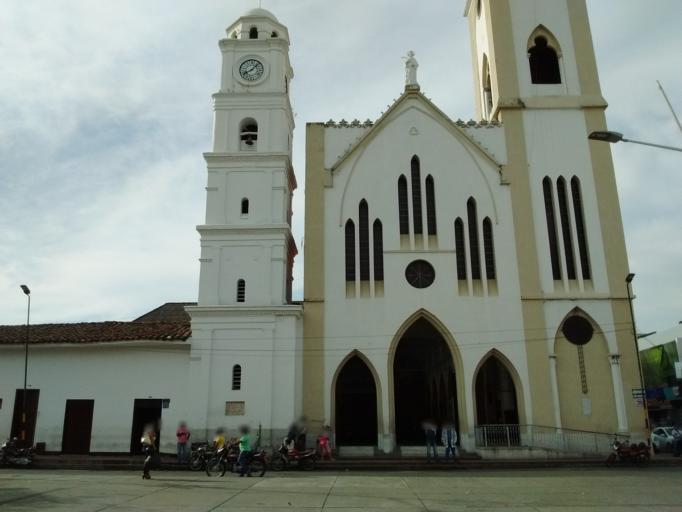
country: CO
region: Valle del Cauca
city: Tulua
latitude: 4.0854
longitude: -76.1975
